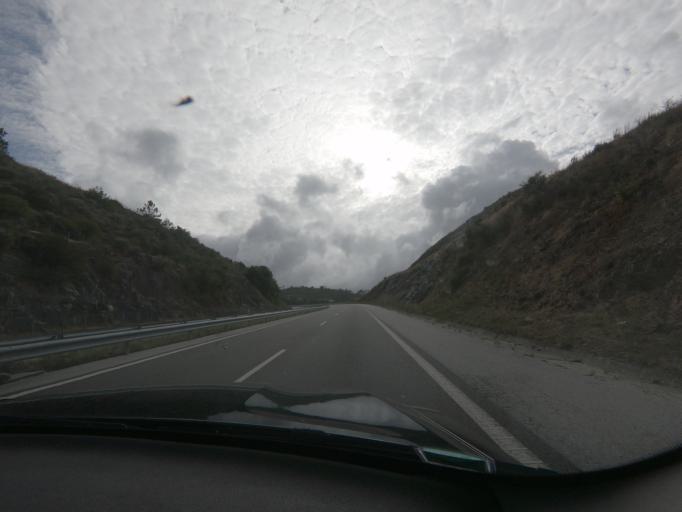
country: PT
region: Viseu
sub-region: Lamego
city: Lamego
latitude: 41.0708
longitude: -7.8259
